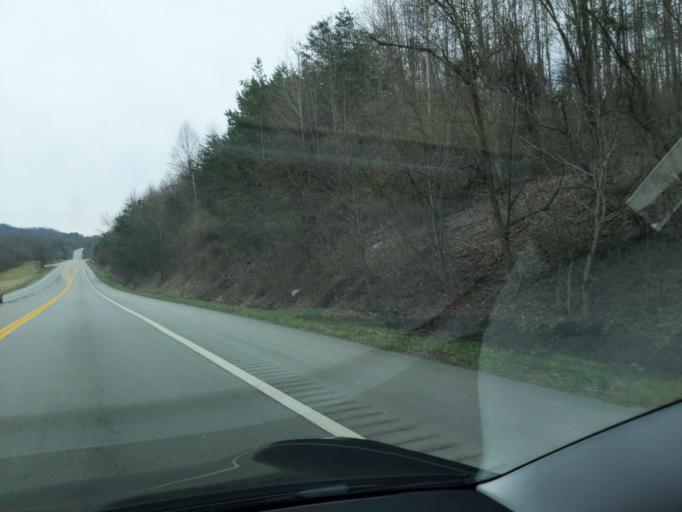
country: US
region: Kentucky
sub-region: Whitley County
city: Corbin
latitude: 36.9171
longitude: -84.0953
